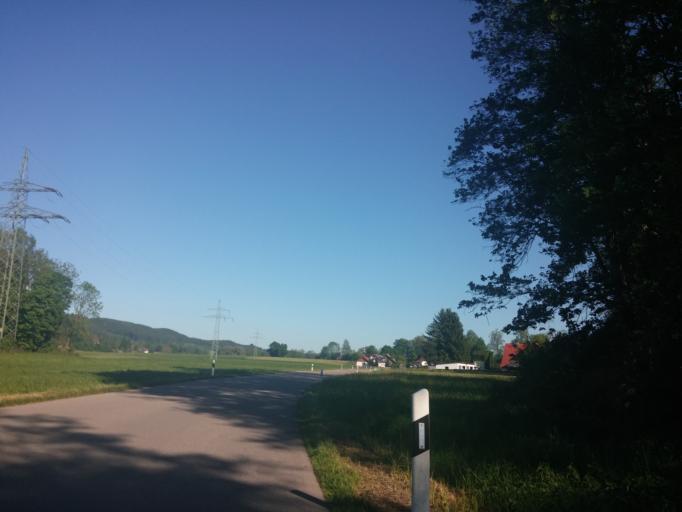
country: DE
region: Bavaria
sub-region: Swabia
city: Lautrach
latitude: 47.8988
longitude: 10.1380
